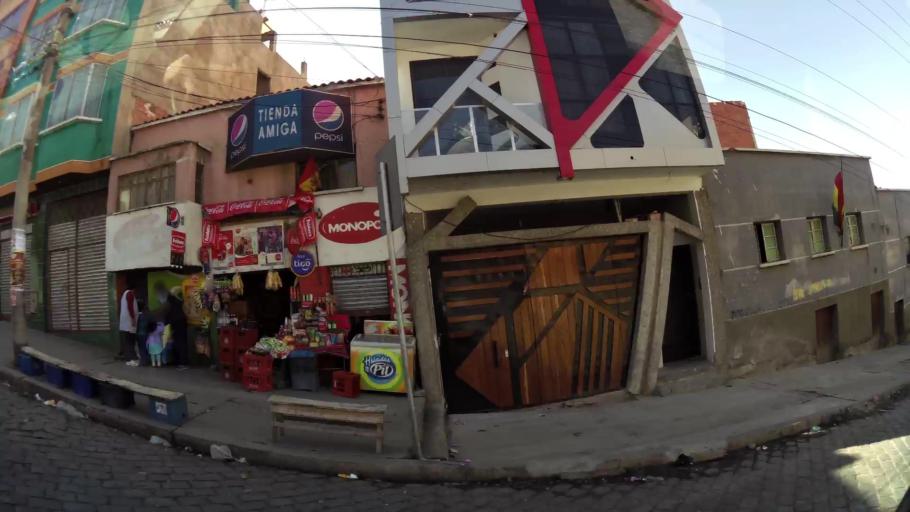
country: BO
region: La Paz
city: La Paz
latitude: -16.4930
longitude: -68.1594
